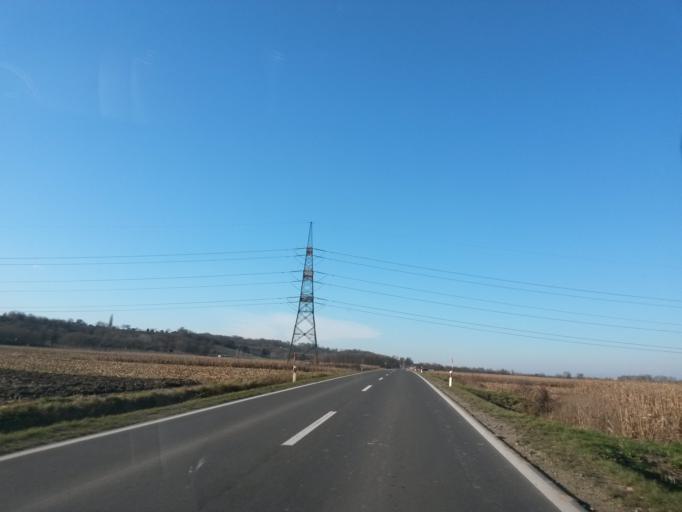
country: HR
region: Koprivnicko-Krizevacka
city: Reka
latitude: 46.2023
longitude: 16.7108
